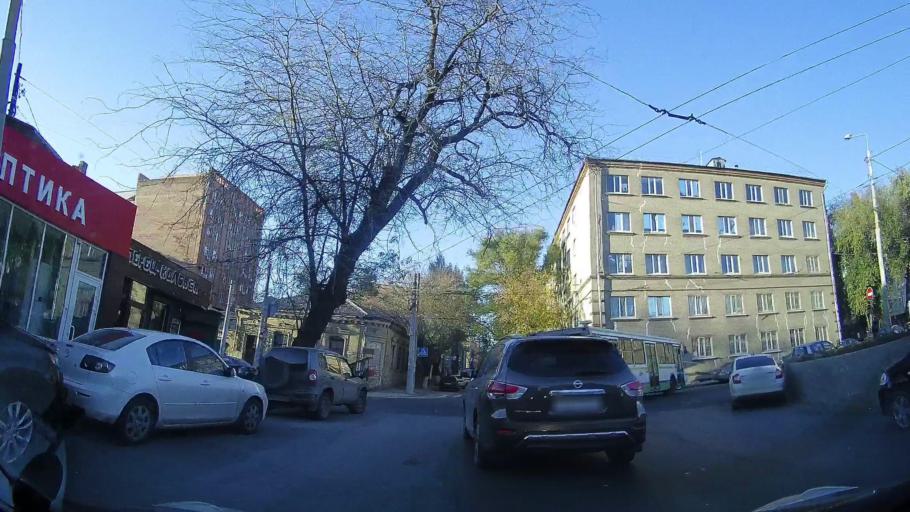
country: RU
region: Rostov
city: Rostov-na-Donu
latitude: 47.2167
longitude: 39.7064
